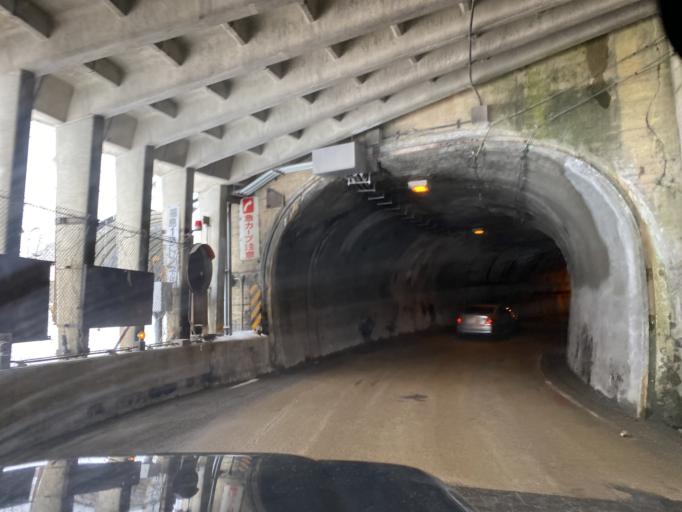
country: JP
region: Gifu
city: Takayama
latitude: 36.1297
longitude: 136.9111
